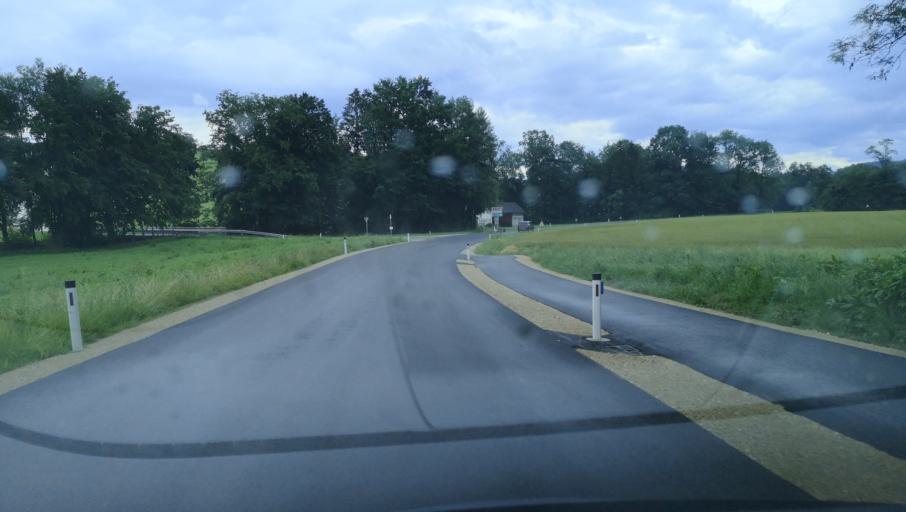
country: AT
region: Lower Austria
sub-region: Politischer Bezirk Amstetten
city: Allhartsberg
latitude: 48.0359
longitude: 14.8190
